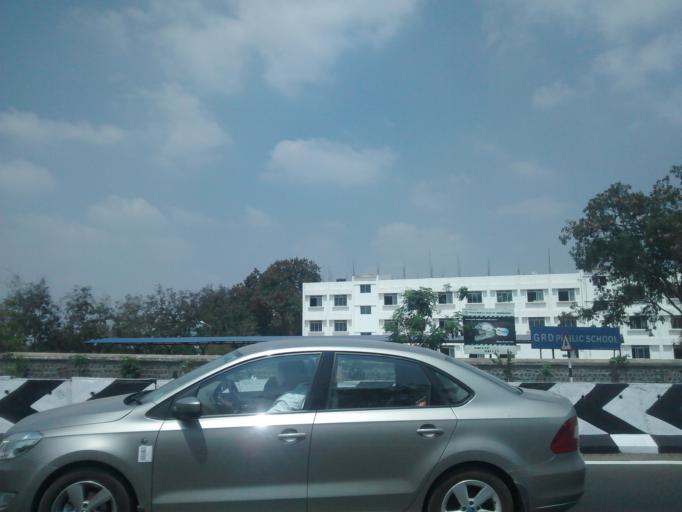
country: IN
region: Tamil Nadu
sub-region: Coimbatore
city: Singanallur
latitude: 11.0322
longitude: 77.0303
